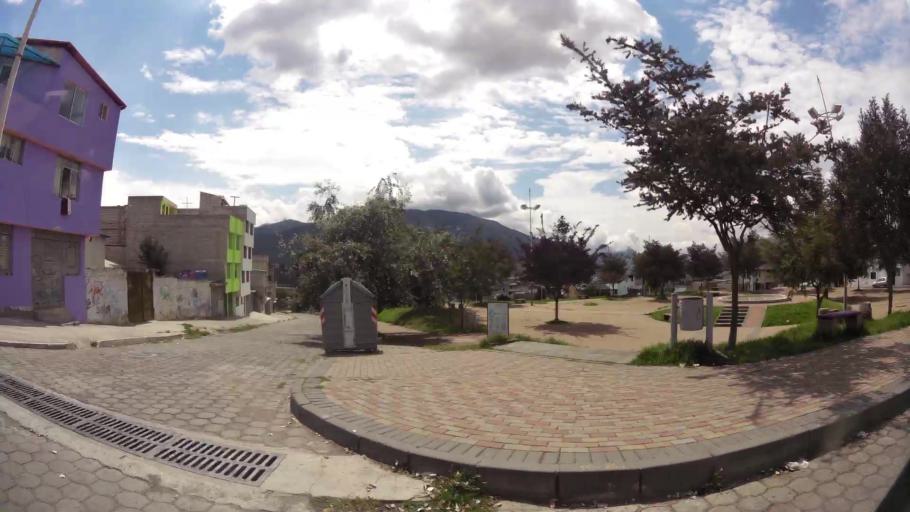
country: EC
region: Pichincha
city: Quito
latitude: -0.0891
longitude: -78.4491
